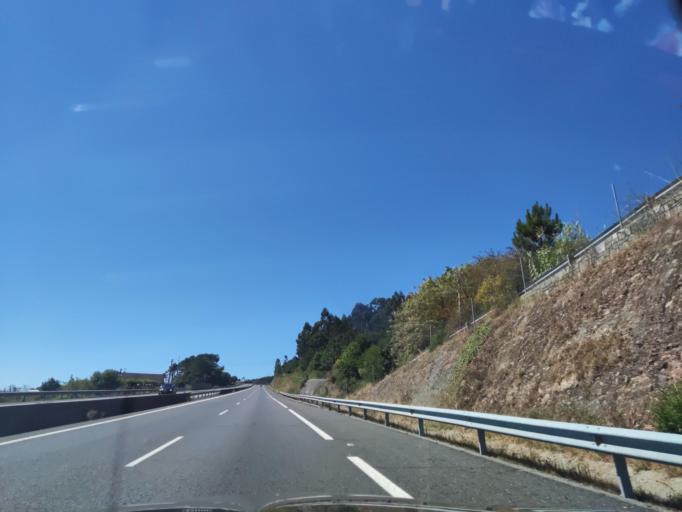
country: ES
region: Galicia
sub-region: Provincia da Coruna
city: Boiro
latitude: 42.6528
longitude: -8.9015
